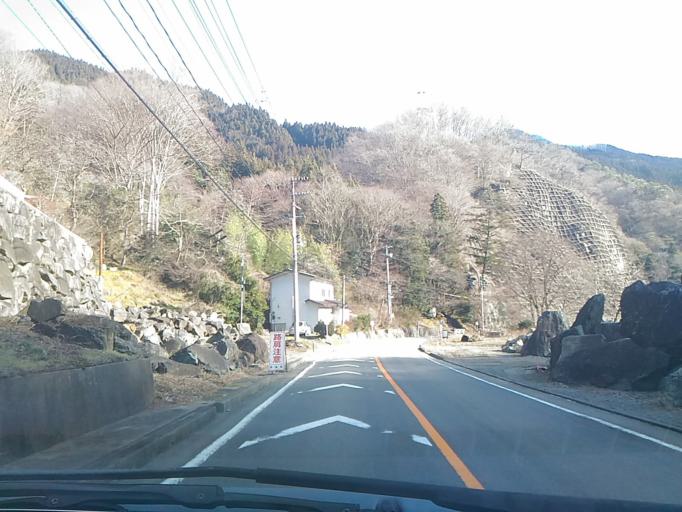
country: JP
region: Fukushima
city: Ishikawa
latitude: 37.0533
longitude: 140.6096
